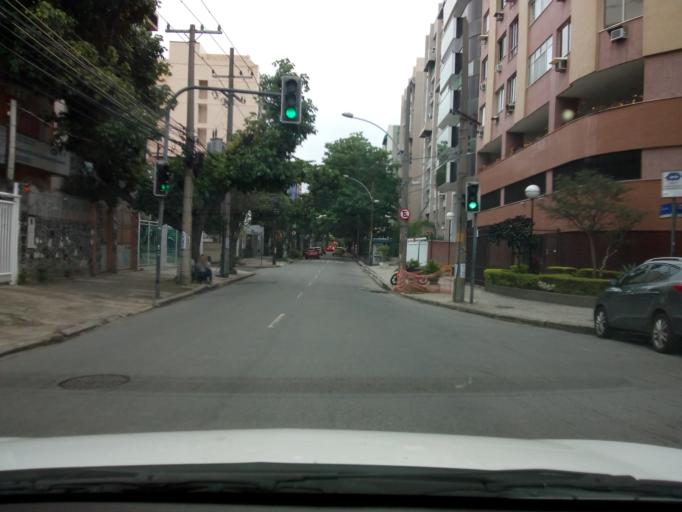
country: BR
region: Rio de Janeiro
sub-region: Rio De Janeiro
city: Rio de Janeiro
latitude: -22.9180
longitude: -43.2202
